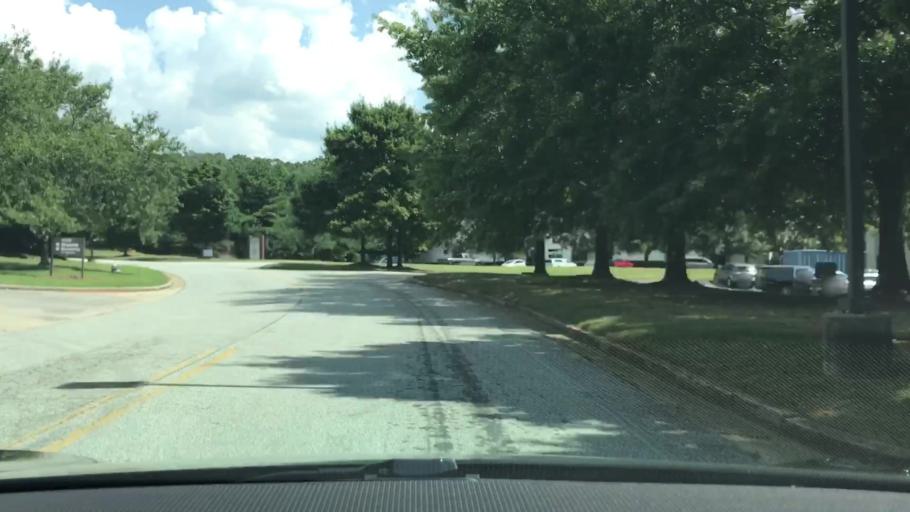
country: US
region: Georgia
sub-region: Gwinnett County
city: Buford
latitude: 34.1004
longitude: -84.0060
